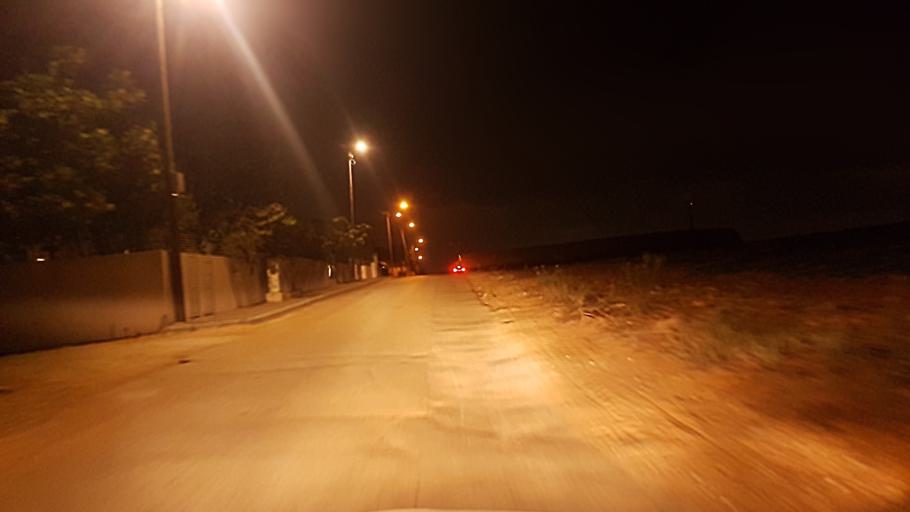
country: IL
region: Central District
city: Hod HaSharon
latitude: 32.1597
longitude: 34.8722
